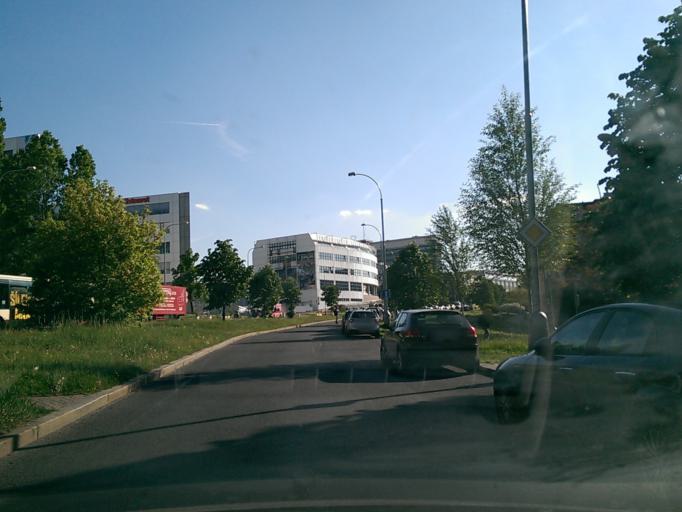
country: CZ
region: Praha
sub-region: Praha 2
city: Vysehrad
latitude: 50.0529
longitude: 14.4303
